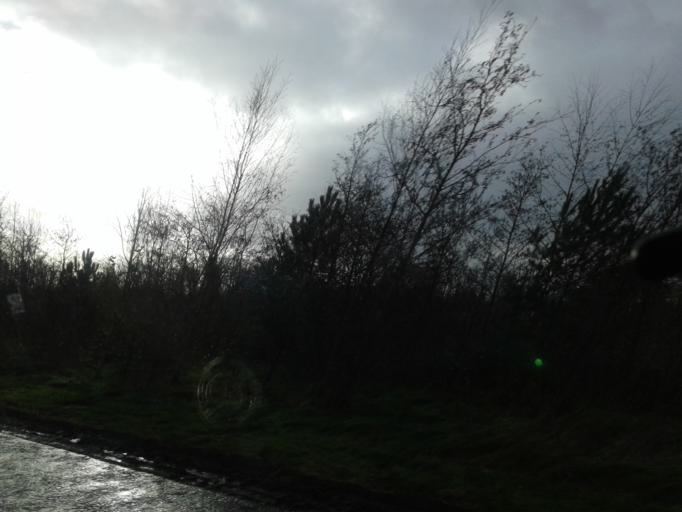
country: IE
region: Leinster
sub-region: An Mhi
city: Ashbourne
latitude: 53.4639
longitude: -6.3587
